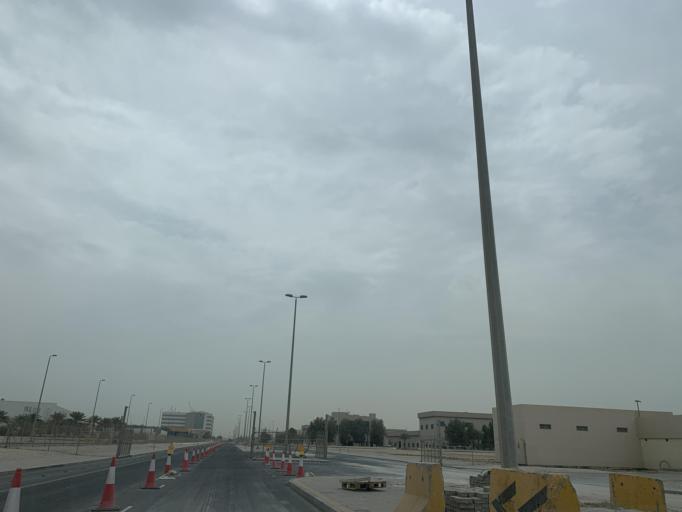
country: BH
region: Muharraq
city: Al Hadd
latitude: 26.2196
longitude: 50.6674
